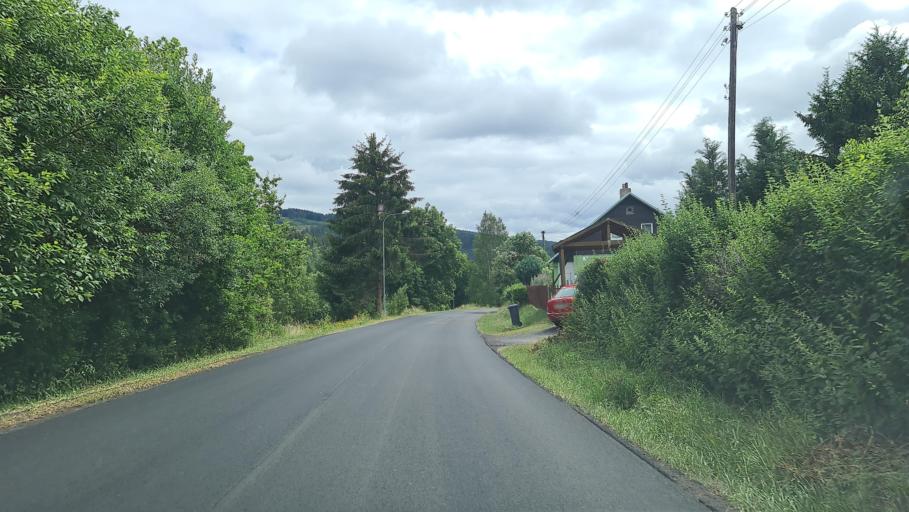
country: CZ
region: Karlovarsky
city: Kraslice
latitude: 50.3649
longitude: 12.5228
